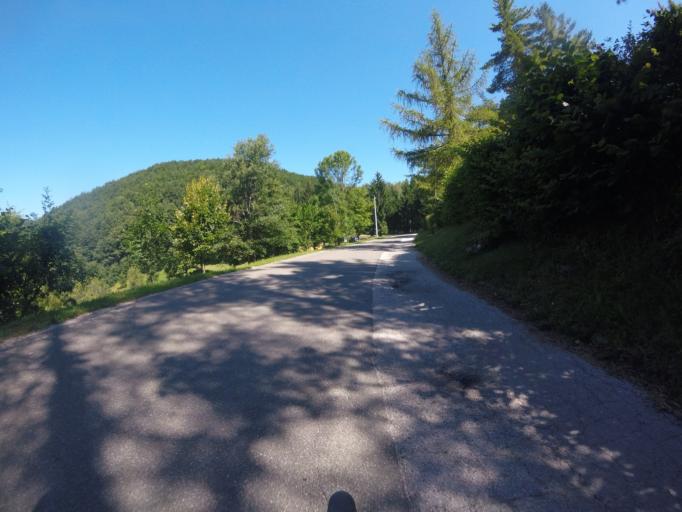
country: SI
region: Brezice
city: Brezice
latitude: 45.8183
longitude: 15.5292
